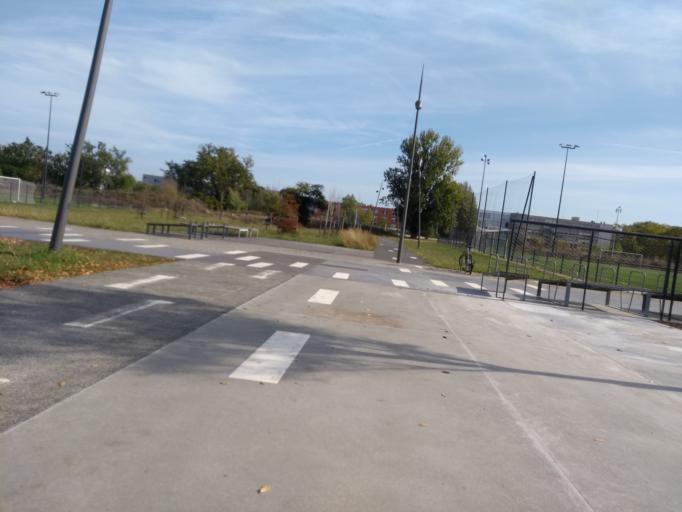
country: FR
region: Aquitaine
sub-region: Departement de la Gironde
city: Talence
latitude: 44.8016
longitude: -0.6058
